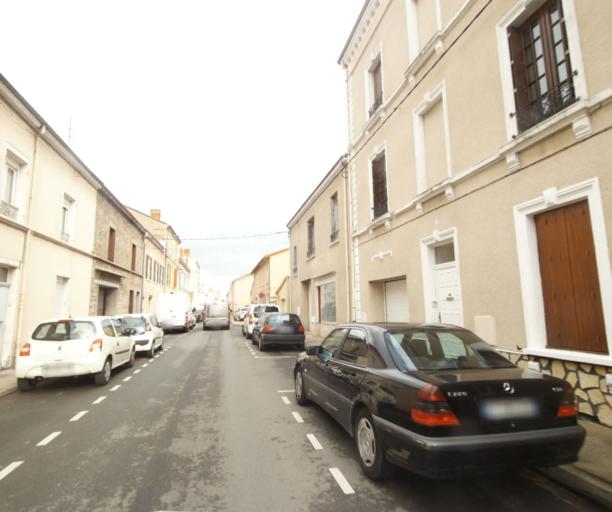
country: FR
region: Rhone-Alpes
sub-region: Departement de la Loire
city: Roanne
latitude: 46.0369
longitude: 4.0583
